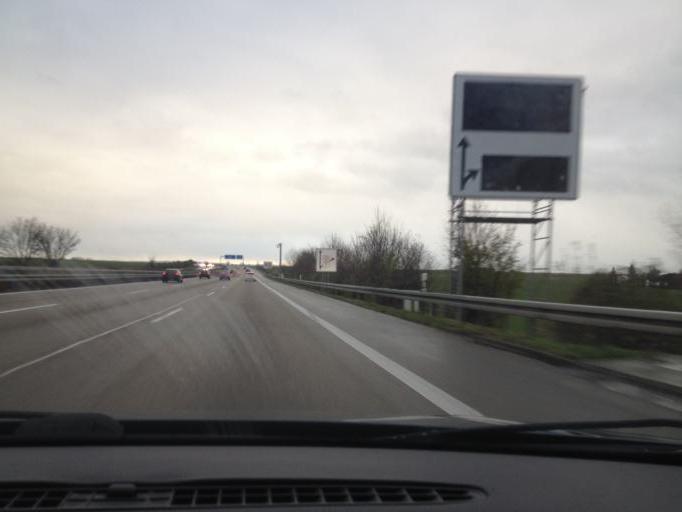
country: DE
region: Baden-Wuerttemberg
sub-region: Regierungsbezirk Stuttgart
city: Moglingen
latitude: 48.8673
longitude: 9.1319
